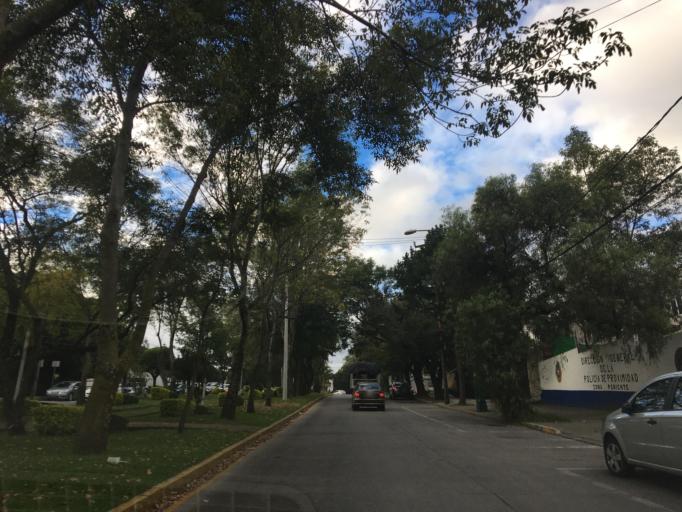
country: MX
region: Mexico City
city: Polanco
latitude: 19.4219
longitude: -99.2077
